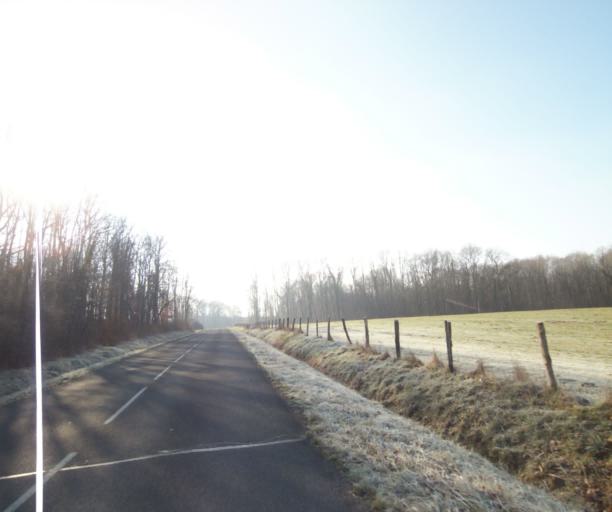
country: FR
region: Champagne-Ardenne
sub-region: Departement de la Haute-Marne
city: Wassy
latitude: 48.4832
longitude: 4.9353
